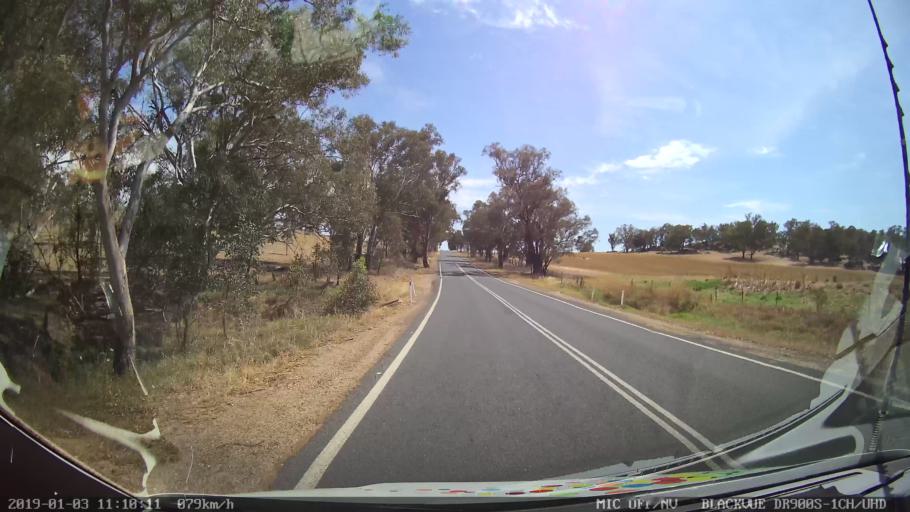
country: AU
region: New South Wales
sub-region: Young
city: Young
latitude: -34.2296
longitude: 148.2577
